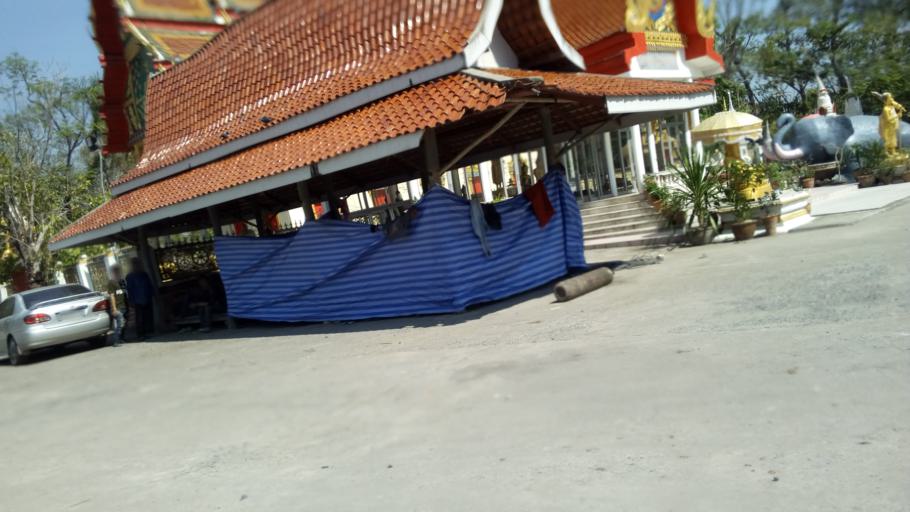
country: TH
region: Pathum Thani
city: Ban Rangsit
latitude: 14.0537
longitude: 100.8255
